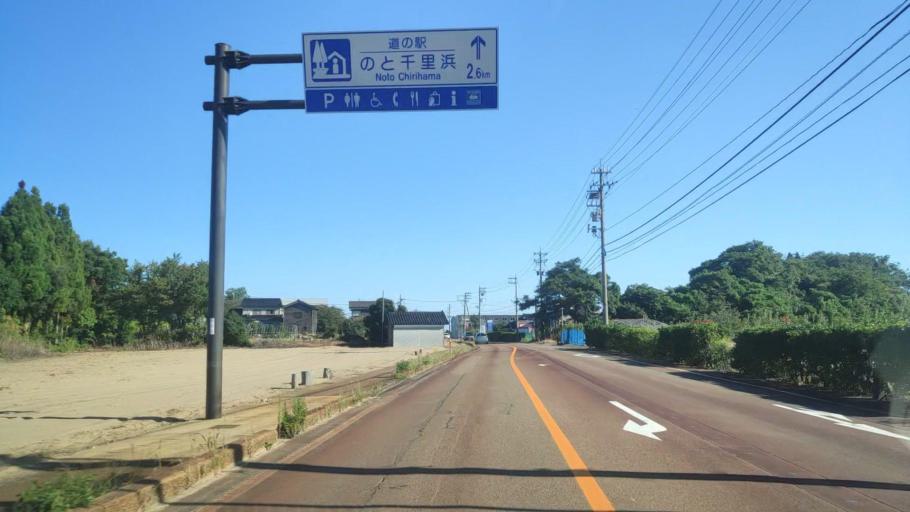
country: JP
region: Ishikawa
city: Hakui
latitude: 36.8699
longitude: 136.7729
